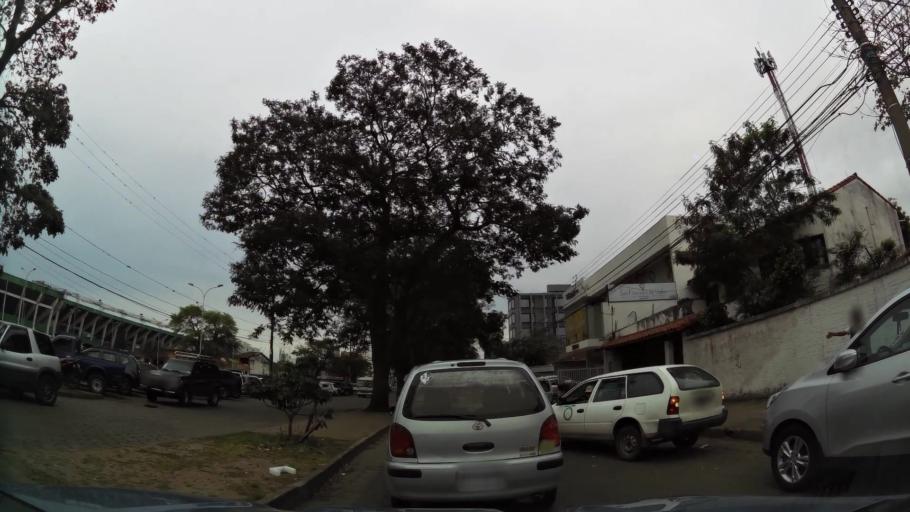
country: BO
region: Santa Cruz
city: Santa Cruz de la Sierra
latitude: -17.7979
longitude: -63.1851
